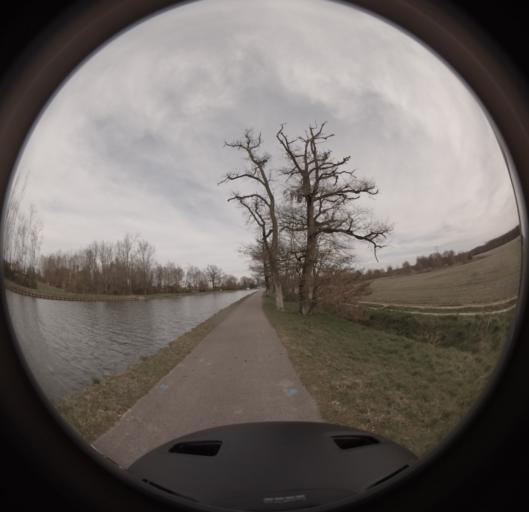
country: FR
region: Midi-Pyrenees
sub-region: Departement du Tarn-et-Garonne
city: Montech
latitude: 43.9832
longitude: 1.2573
